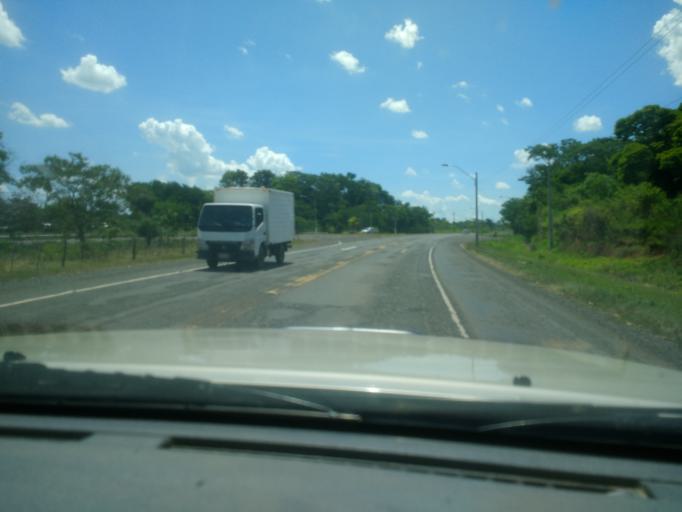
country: PY
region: San Pedro
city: Itacurubi del Rosario
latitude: -24.5255
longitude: -56.8393
